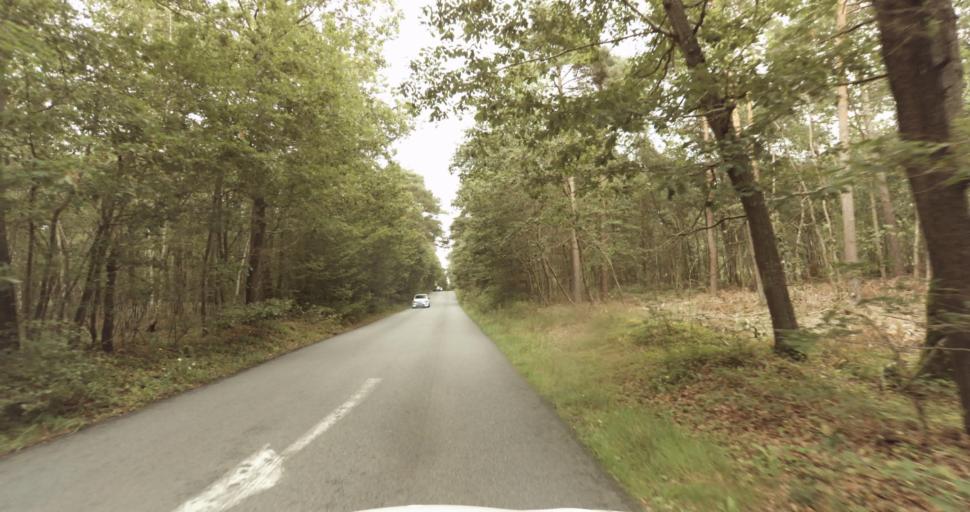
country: FR
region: Haute-Normandie
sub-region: Departement de l'Eure
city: Arnieres-sur-Iton
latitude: 49.0017
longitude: 1.1261
